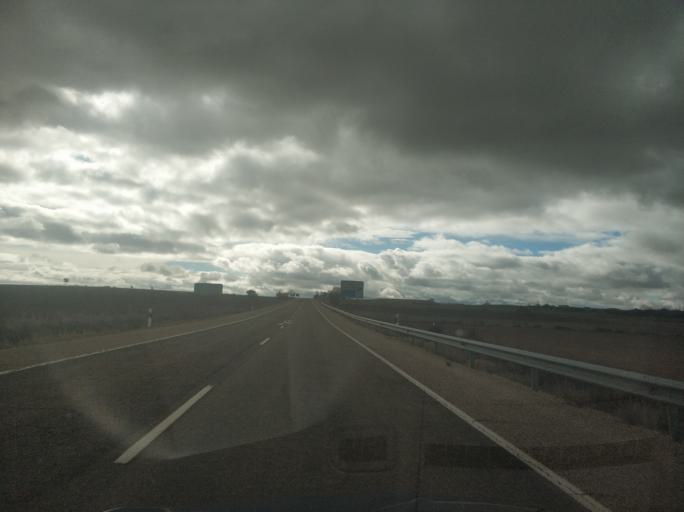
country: ES
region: Castille and Leon
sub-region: Provincia de Zamora
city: Castrillo de la Guarena
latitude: 41.2268
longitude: -5.3128
